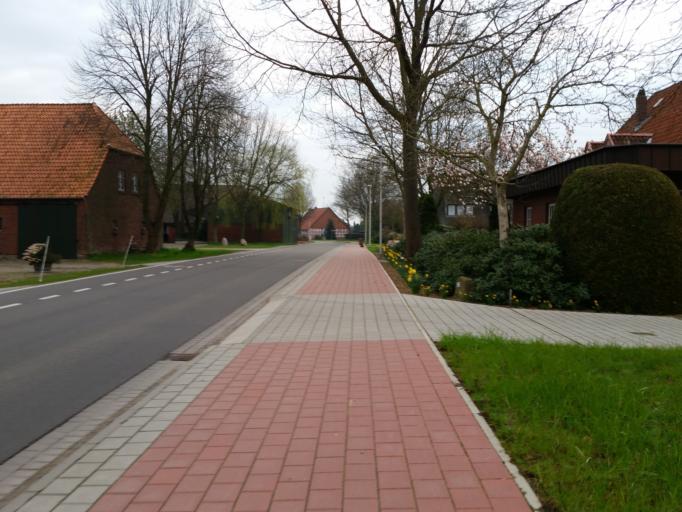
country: DE
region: Lower Saxony
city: Kutenholz
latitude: 53.4874
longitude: 9.2699
